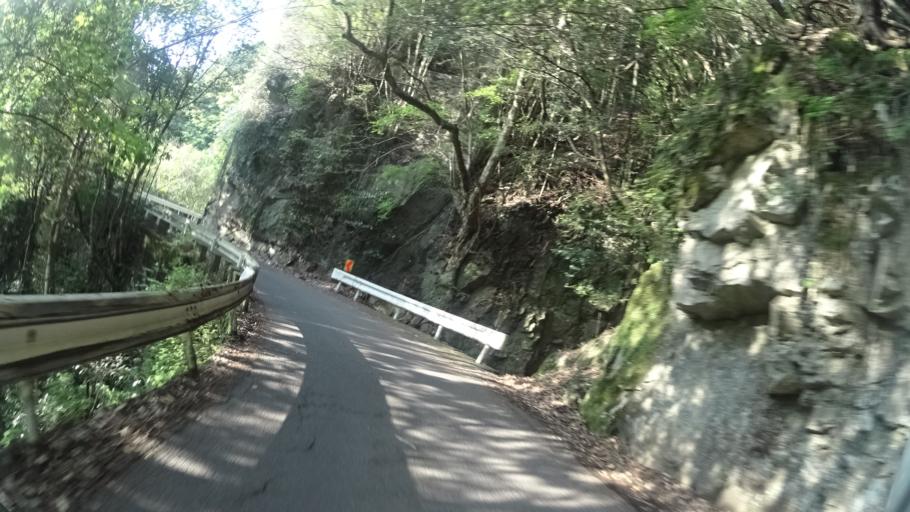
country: JP
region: Tokushima
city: Ikedacho
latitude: 33.9389
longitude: 133.8183
